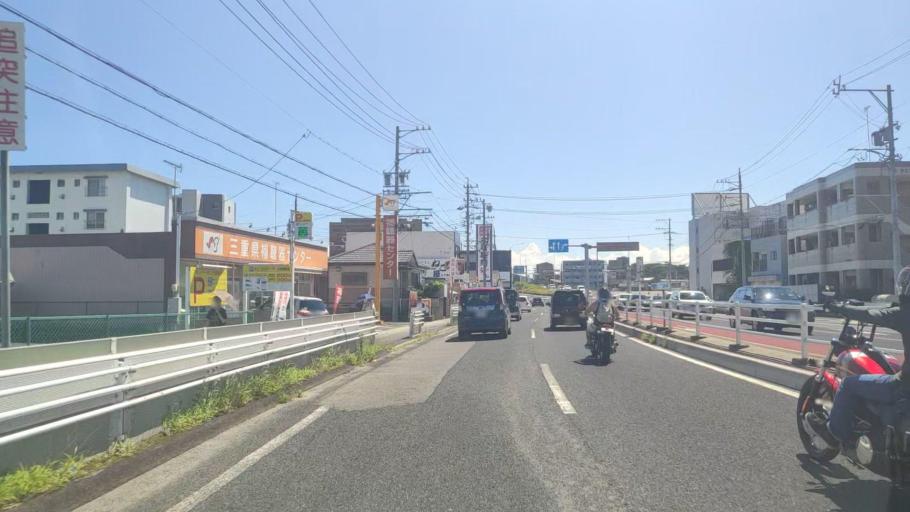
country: JP
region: Mie
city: Tsu-shi
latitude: 34.7435
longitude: 136.5180
